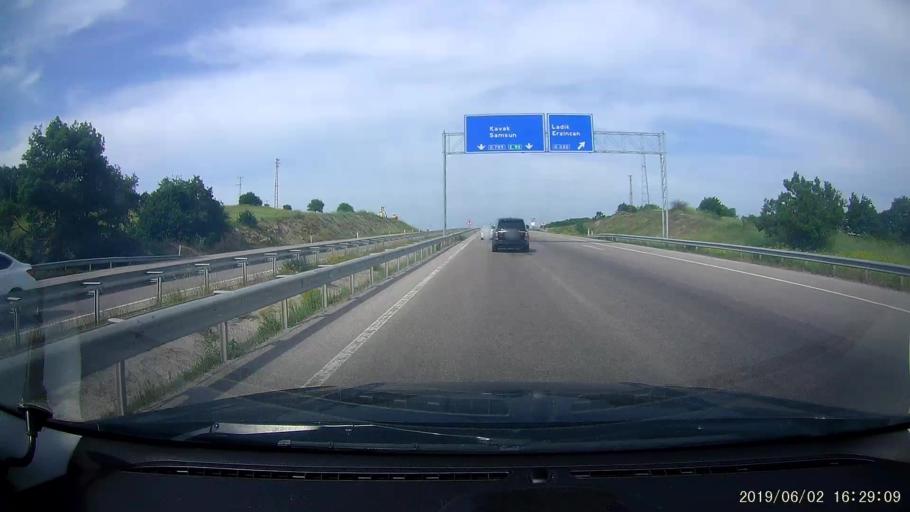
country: TR
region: Samsun
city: Ladik
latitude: 41.0113
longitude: 35.8632
